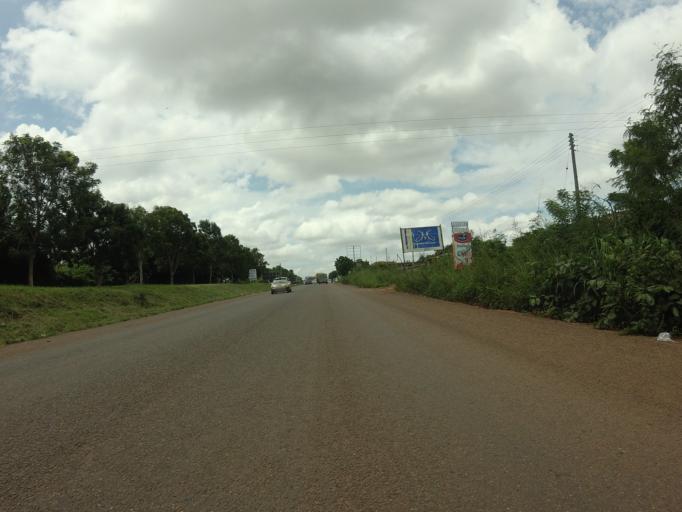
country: GH
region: Eastern
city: Aburi
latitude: 5.8009
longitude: -0.1267
